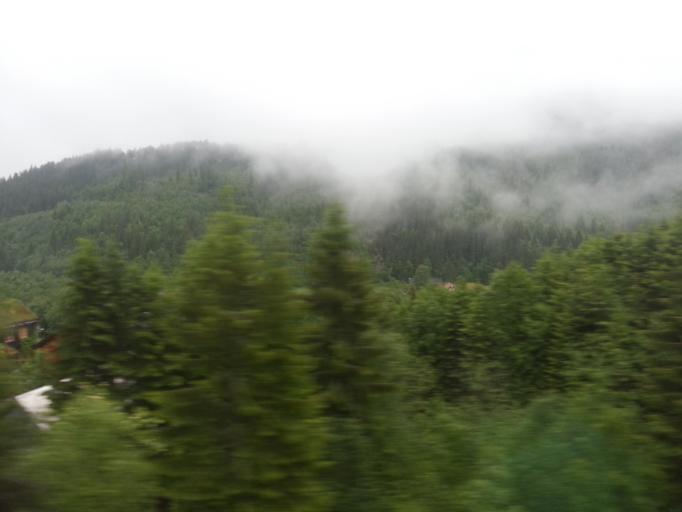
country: NO
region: Sor-Trondelag
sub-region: Midtre Gauldal
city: Storen
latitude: 63.0234
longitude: 10.2472
